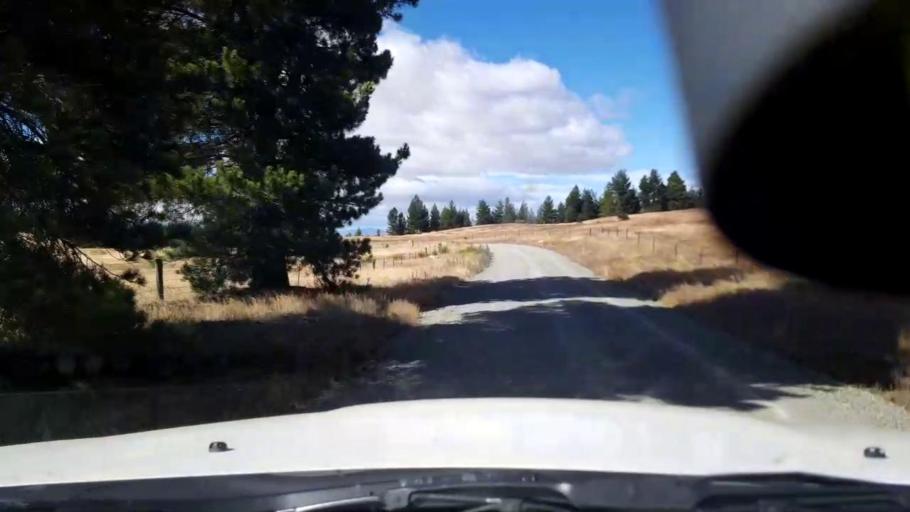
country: NZ
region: Canterbury
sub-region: Timaru District
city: Pleasant Point
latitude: -44.0099
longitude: 170.4727
